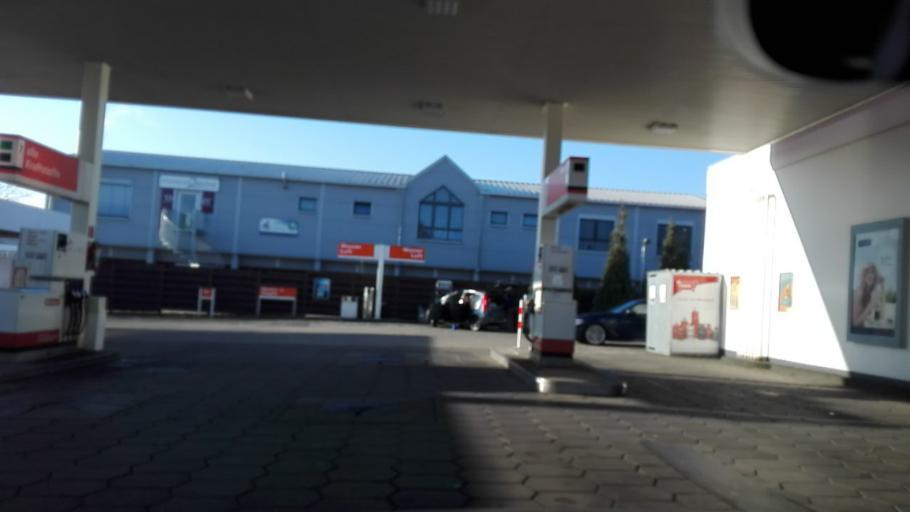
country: DE
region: North Rhine-Westphalia
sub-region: Regierungsbezirk Arnsberg
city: Holzwickede
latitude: 51.5151
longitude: 7.6204
